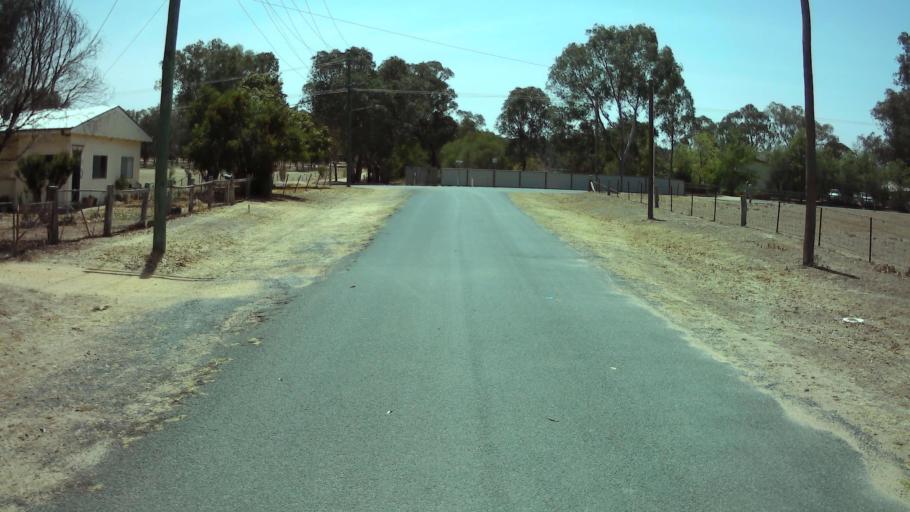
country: AU
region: New South Wales
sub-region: Weddin
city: Grenfell
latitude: -33.8891
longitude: 148.1694
